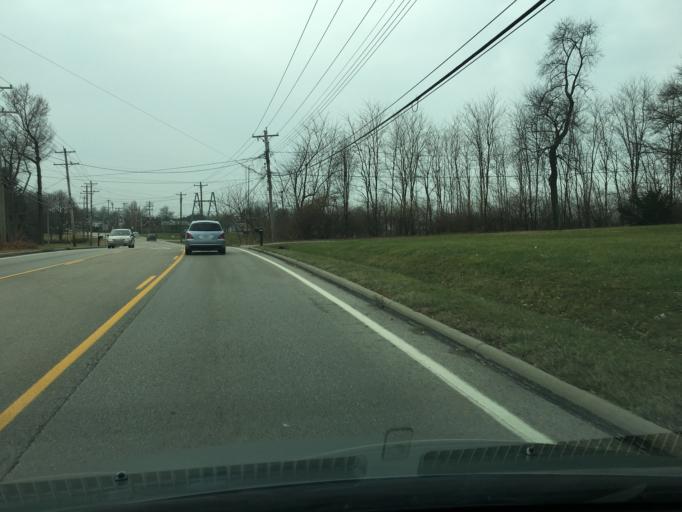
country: US
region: Ohio
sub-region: Hamilton County
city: Highpoint
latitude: 39.3082
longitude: -84.3839
